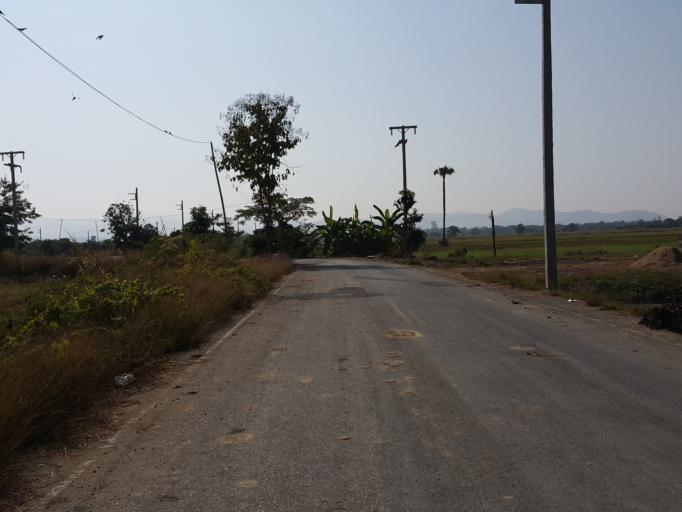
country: TH
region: Lamphun
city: Ban Thi
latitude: 18.6847
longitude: 99.1346
